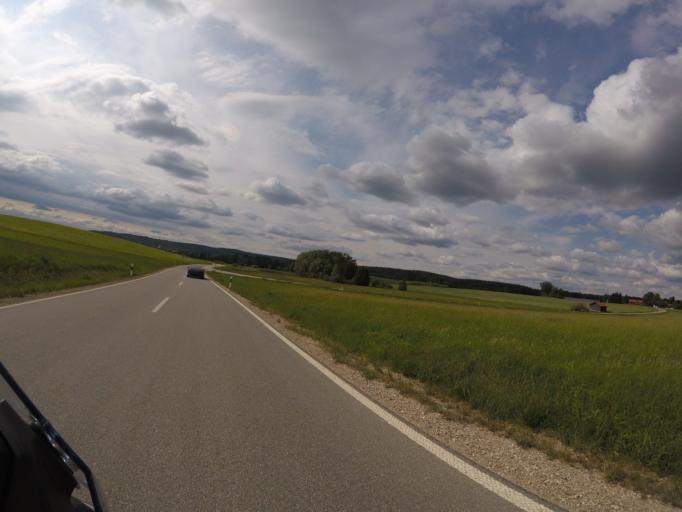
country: DE
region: Bavaria
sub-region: Upper Bavaria
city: Egling
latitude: 47.8834
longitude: 11.5189
